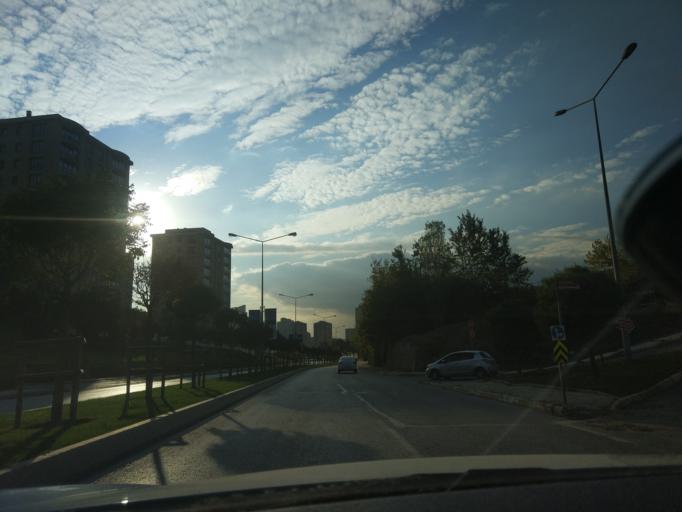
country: TR
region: Istanbul
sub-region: Atasehir
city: Atasehir
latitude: 40.9877
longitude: 29.1176
